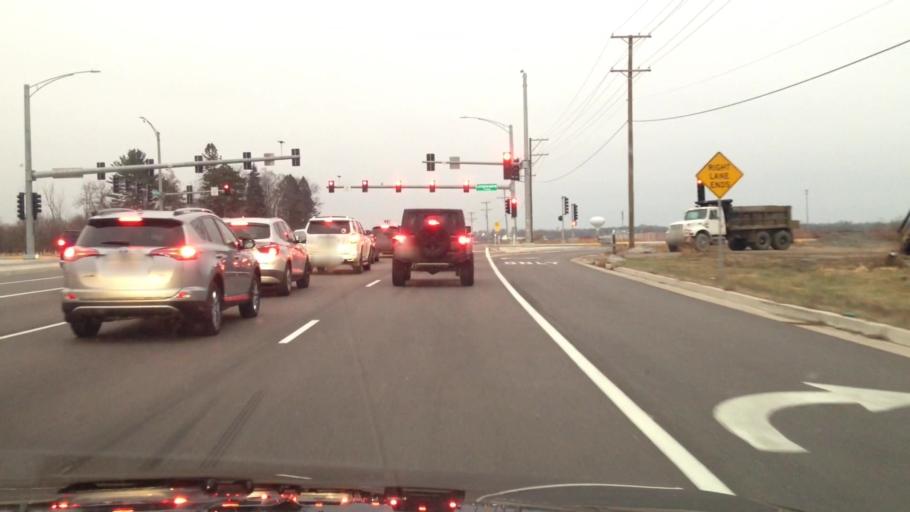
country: US
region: Illinois
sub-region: McHenry County
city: Lake in the Hills
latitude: 42.1407
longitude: -88.3359
